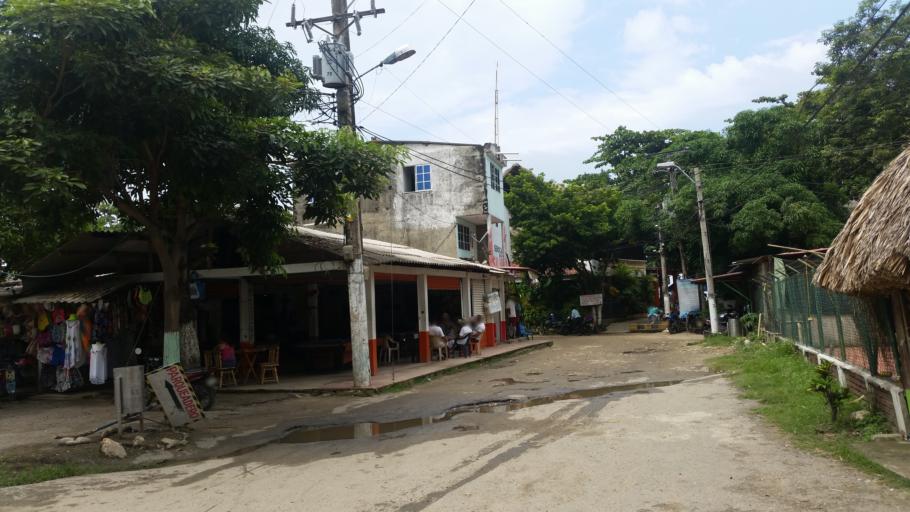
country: CO
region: Magdalena
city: Santa Marta
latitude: 11.2619
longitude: -73.7685
